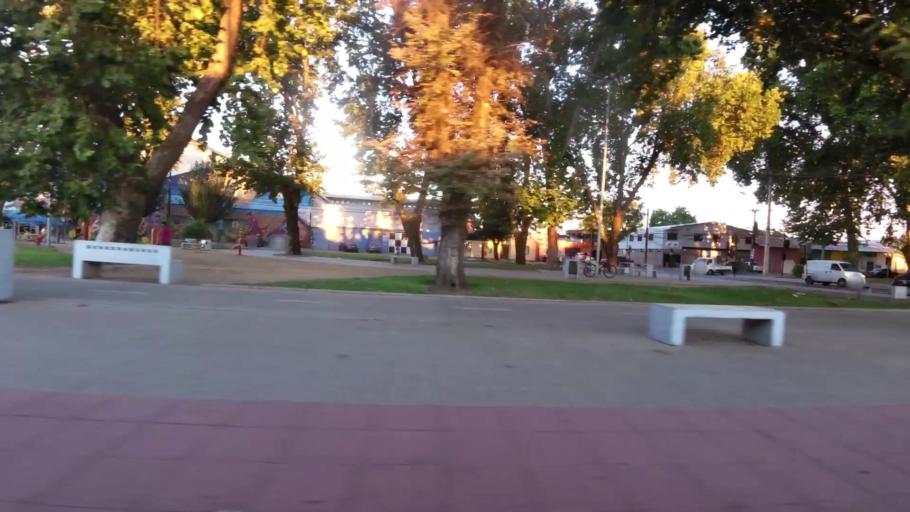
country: CL
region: Maule
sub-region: Provincia de Curico
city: Curico
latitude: -34.9901
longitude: -71.2338
